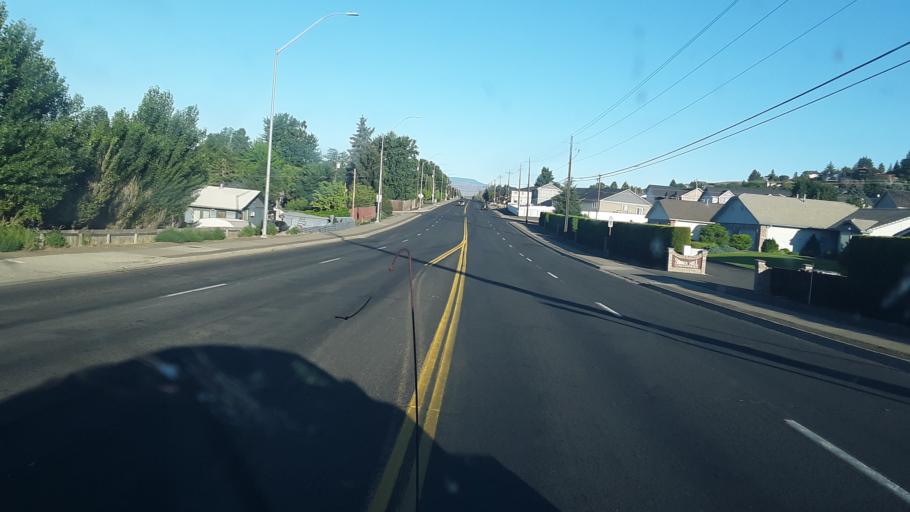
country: US
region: Washington
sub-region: Yakima County
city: West Valley
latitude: 46.6002
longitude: -120.6050
